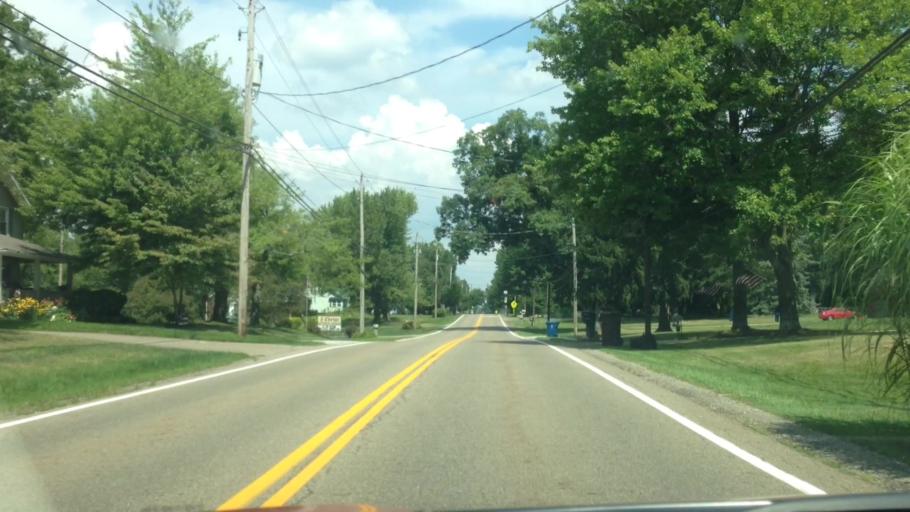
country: US
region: Ohio
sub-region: Stark County
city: Massillon
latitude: 40.8317
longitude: -81.5123
